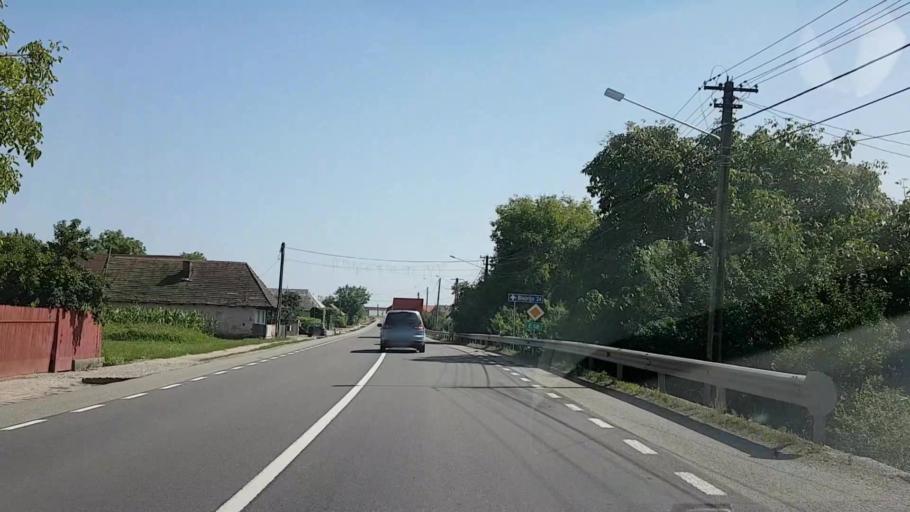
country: RO
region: Bistrita-Nasaud
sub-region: Comuna Sieu-Odorhei
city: Sieu-Odorhei
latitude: 47.1400
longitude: 24.3066
